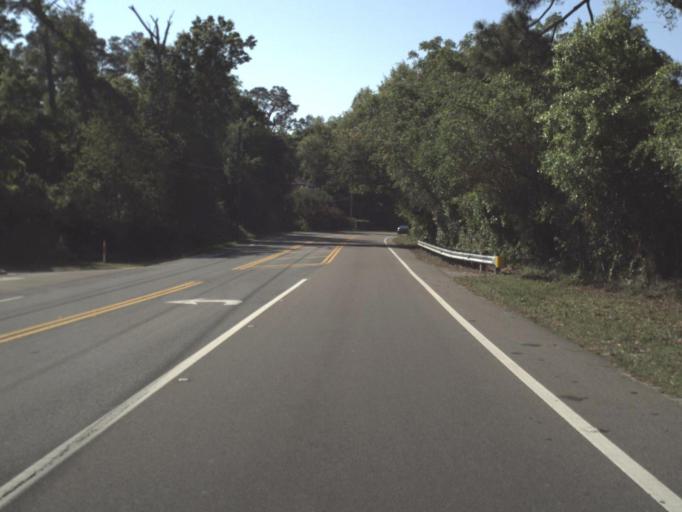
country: US
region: Florida
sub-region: Escambia County
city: Ferry Pass
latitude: 30.5249
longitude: -87.1839
